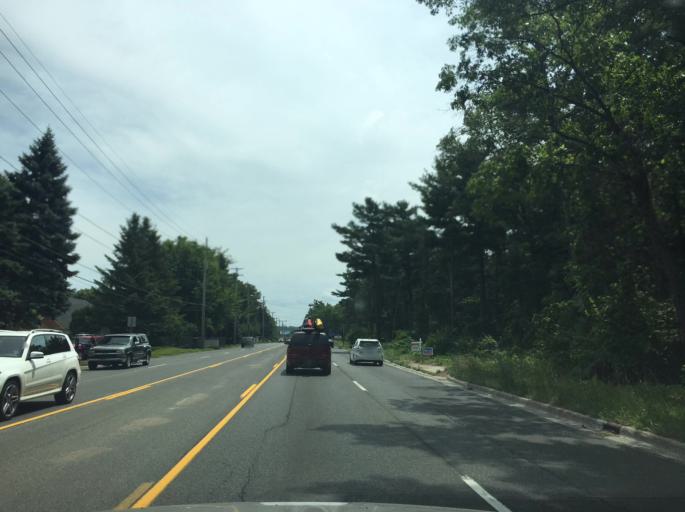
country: US
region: Michigan
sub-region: Grand Traverse County
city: Traverse City
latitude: 44.7515
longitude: -85.5651
